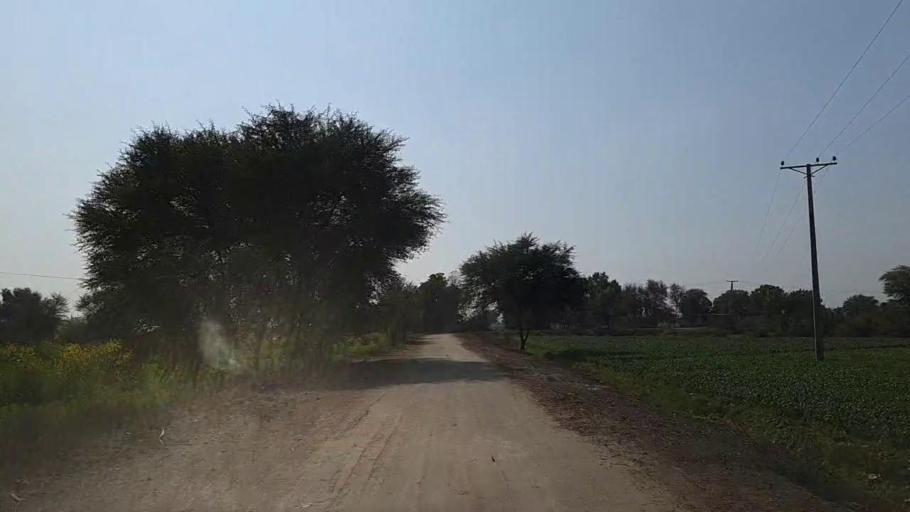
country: PK
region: Sindh
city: Nawabshah
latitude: 26.2484
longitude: 68.4846
